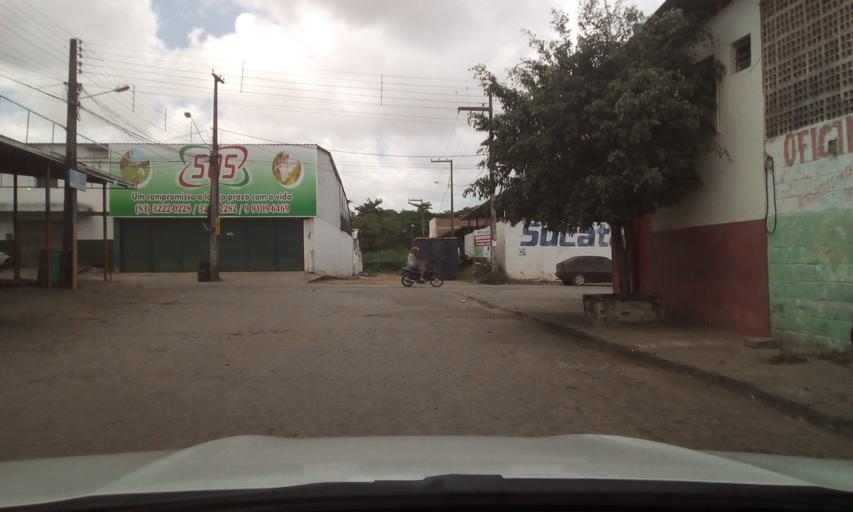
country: BR
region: Paraiba
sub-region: Joao Pessoa
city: Joao Pessoa
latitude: -7.1297
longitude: -34.8879
